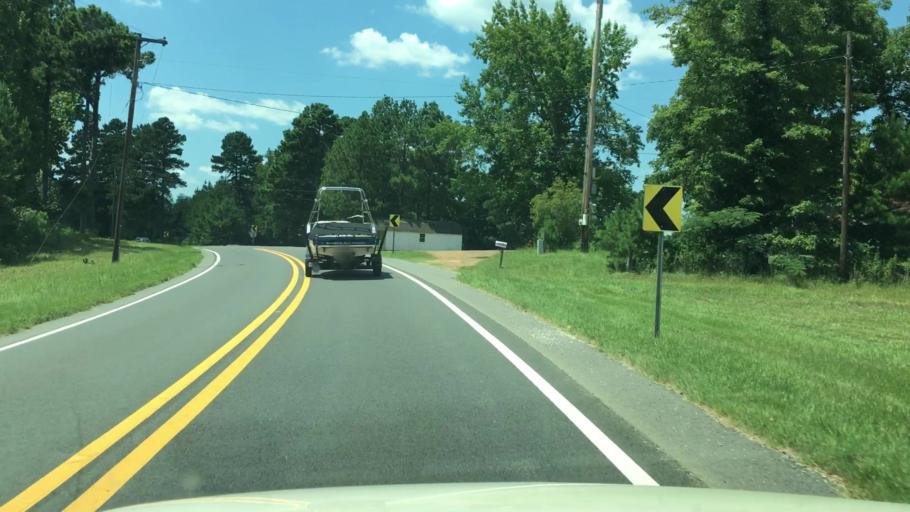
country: US
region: Arkansas
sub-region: Garland County
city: Lake Hamilton
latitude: 34.2774
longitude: -93.1514
